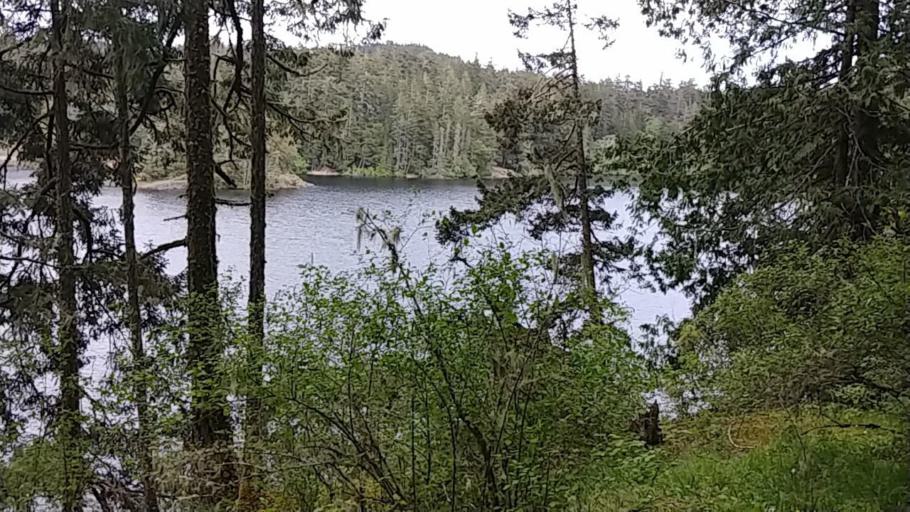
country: CA
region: British Columbia
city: Metchosin
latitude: 48.3631
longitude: -123.6036
